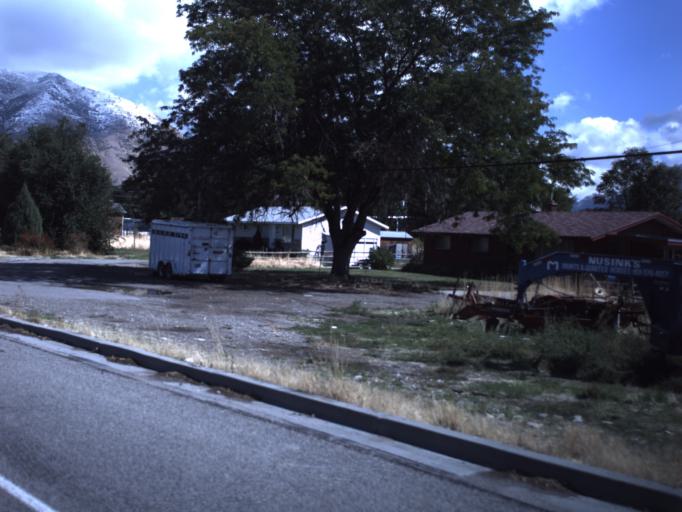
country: US
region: Utah
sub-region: Utah County
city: Springville
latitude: 40.1424
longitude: -111.6119
